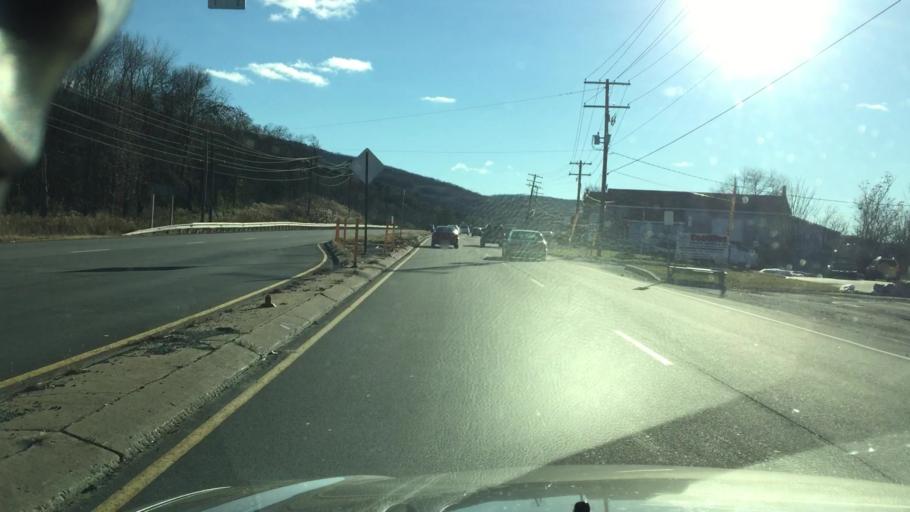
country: US
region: Pennsylvania
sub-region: Luzerne County
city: Ashley
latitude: 41.2209
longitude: -75.8840
